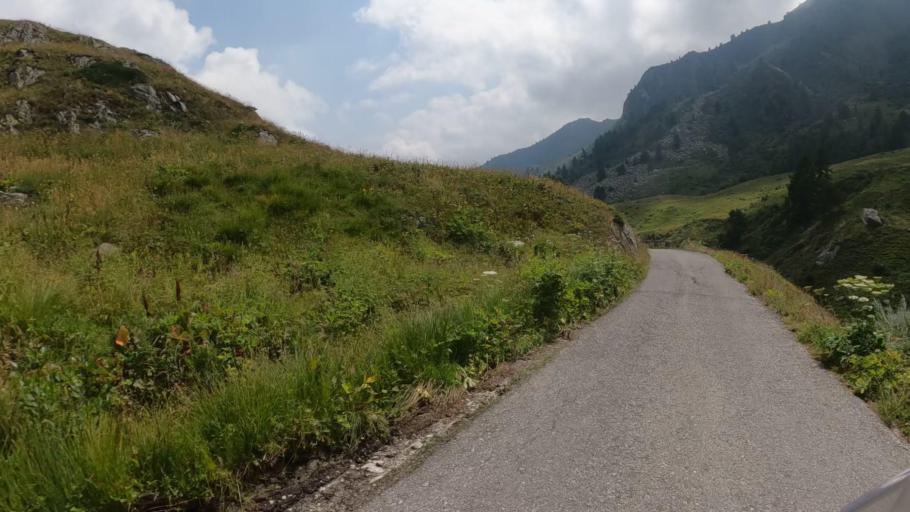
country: IT
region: Piedmont
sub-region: Provincia di Cuneo
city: Campomolino
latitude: 44.3937
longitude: 7.1513
